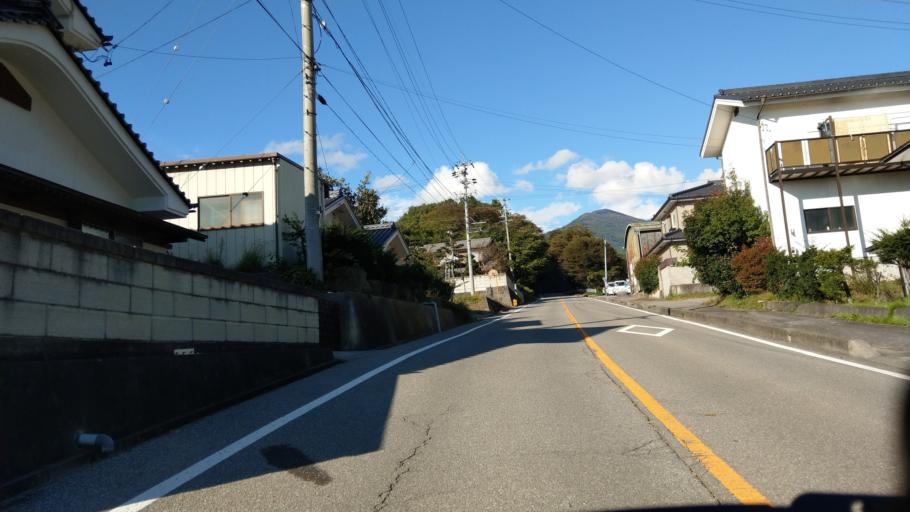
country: JP
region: Nagano
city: Komoro
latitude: 36.3453
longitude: 138.4288
